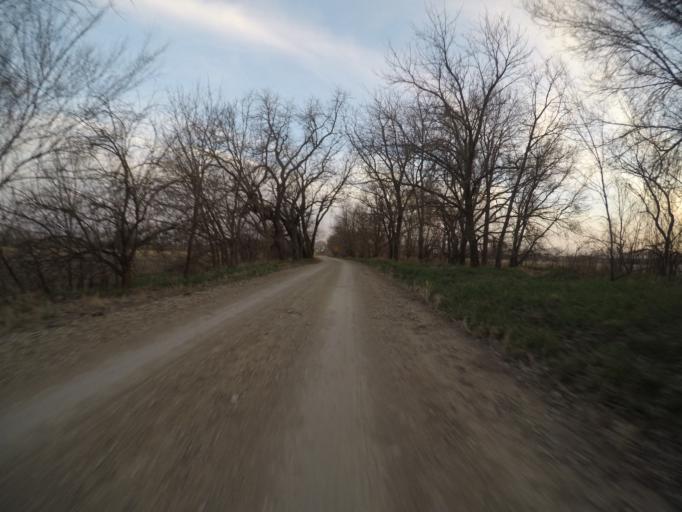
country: US
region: Kansas
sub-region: Riley County
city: Ogden
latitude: 39.1620
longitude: -96.6679
